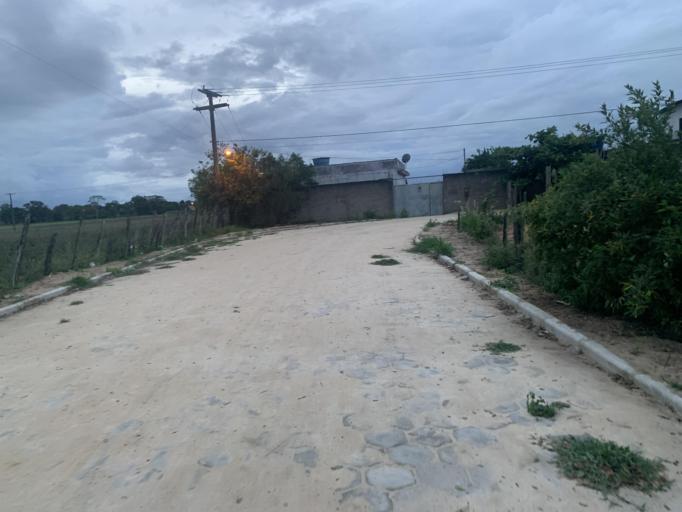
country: BR
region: Bahia
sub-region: Medeiros Neto
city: Medeiros Neto
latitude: -17.3909
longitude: -40.2336
